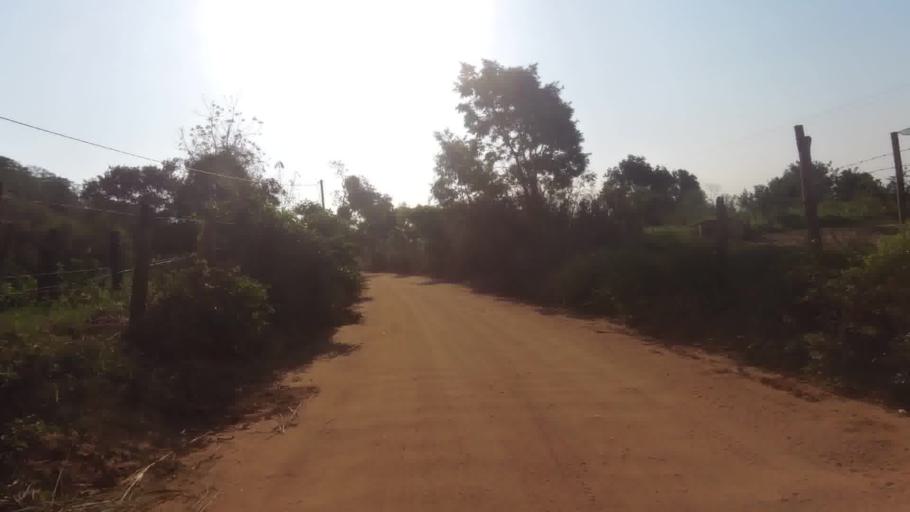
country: BR
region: Espirito Santo
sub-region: Piuma
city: Piuma
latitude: -20.8536
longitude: -40.7580
